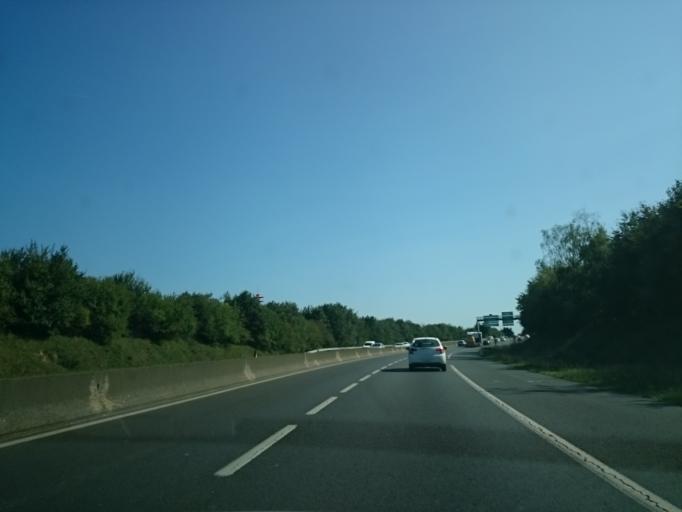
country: FR
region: Pays de la Loire
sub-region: Departement de la Loire-Atlantique
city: Saint-Herblain
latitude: 47.2298
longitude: -1.6223
